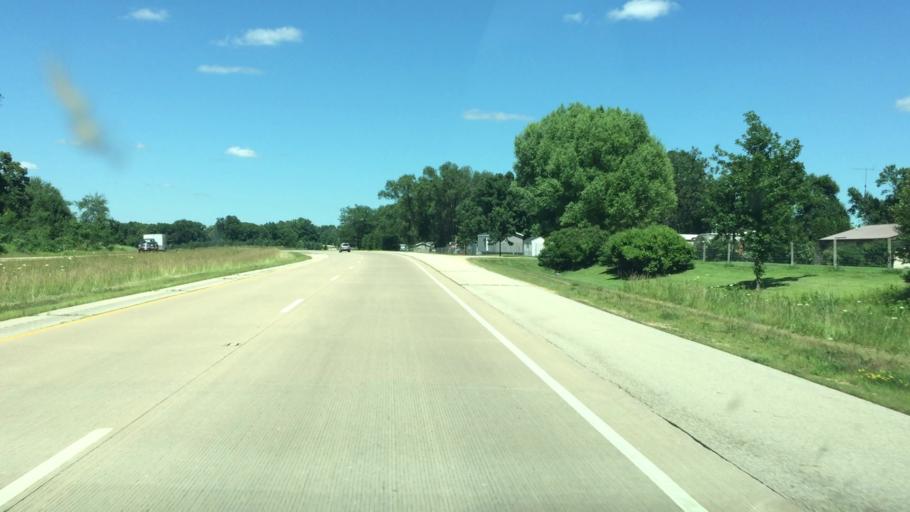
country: US
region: Wisconsin
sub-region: Grant County
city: Platteville
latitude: 42.6911
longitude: -90.5301
